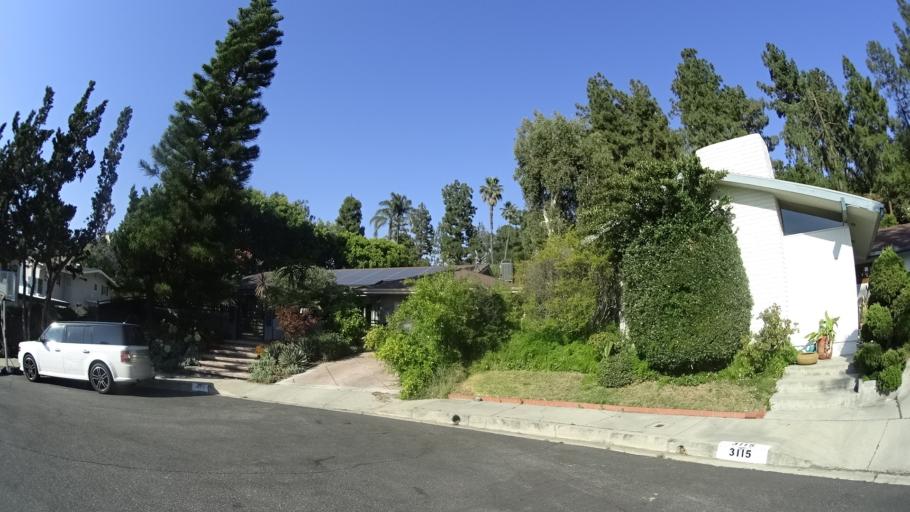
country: US
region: California
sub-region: Los Angeles County
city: Universal City
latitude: 34.1266
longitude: -118.3838
